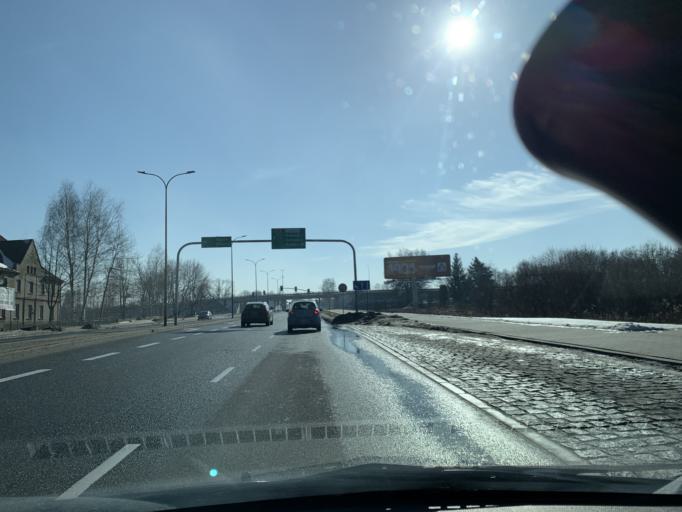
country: PL
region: Silesian Voivodeship
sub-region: Powiat tarnogorski
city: Radzionkow
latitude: 50.3703
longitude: 18.8951
